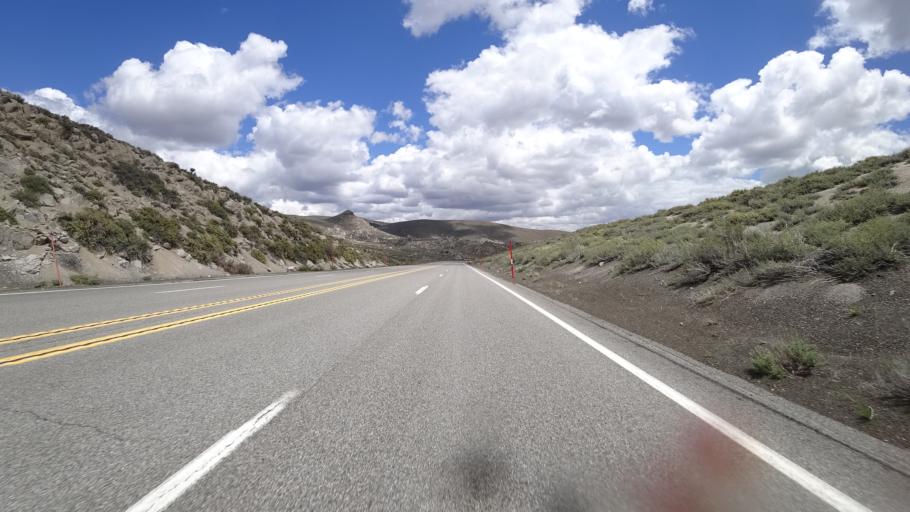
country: US
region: California
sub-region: Mono County
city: Bridgeport
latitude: 38.0835
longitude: -119.1655
